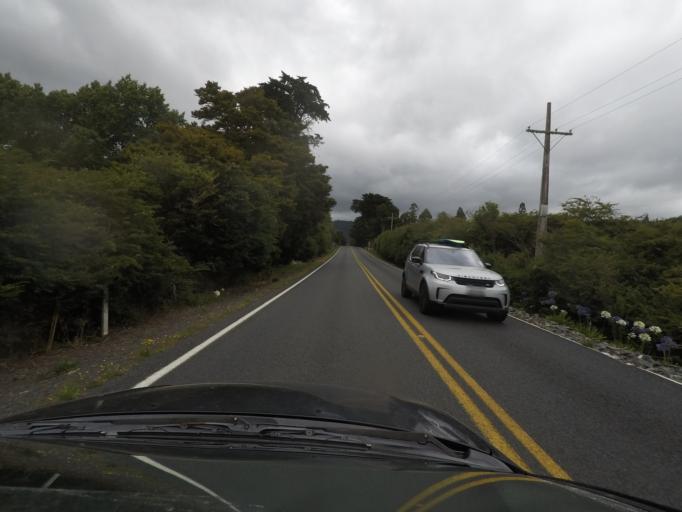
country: NZ
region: Auckland
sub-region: Auckland
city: Wellsford
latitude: -36.2859
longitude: 174.6321
